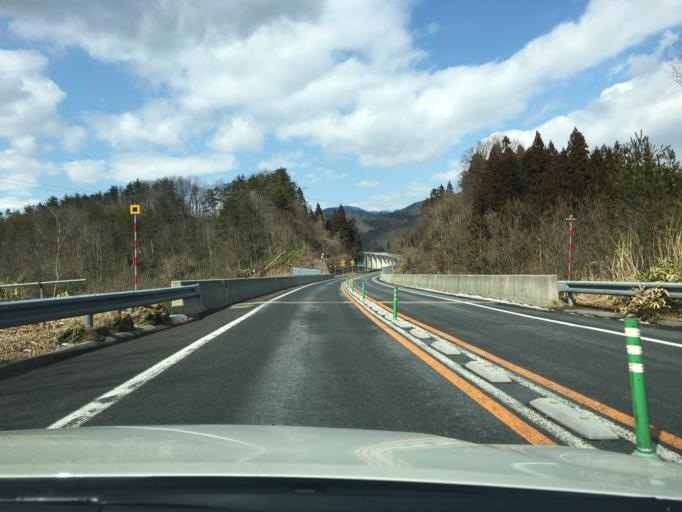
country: JP
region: Yamagata
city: Sagae
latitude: 38.4079
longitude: 140.1911
